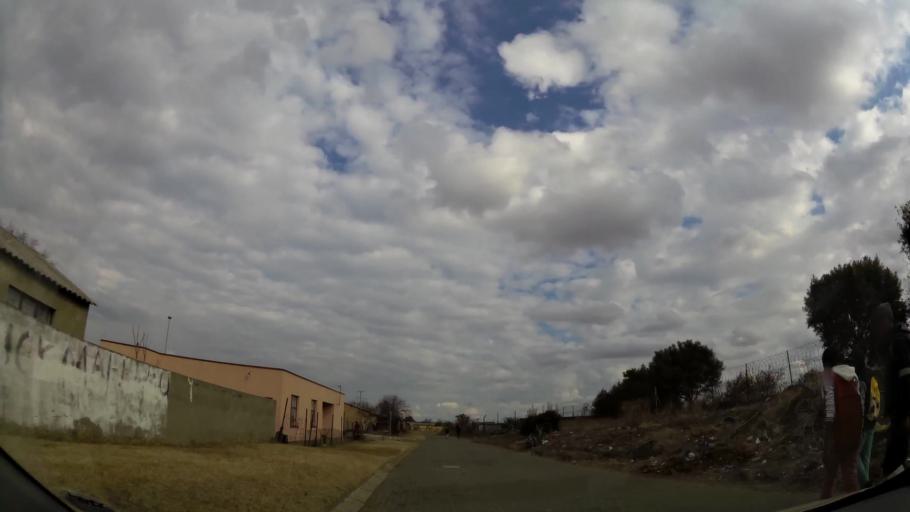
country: ZA
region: Orange Free State
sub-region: Fezile Dabi District Municipality
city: Sasolburg
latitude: -26.8409
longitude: 27.8437
